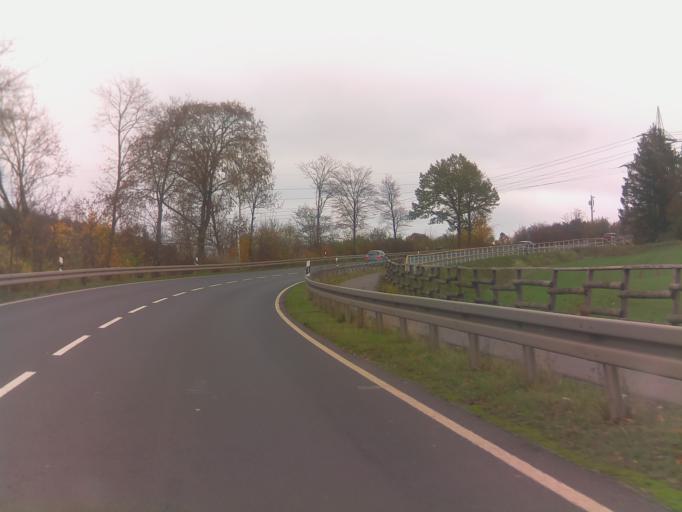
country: DE
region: Hesse
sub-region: Regierungsbezirk Kassel
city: Fulda
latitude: 50.5771
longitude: 9.6860
